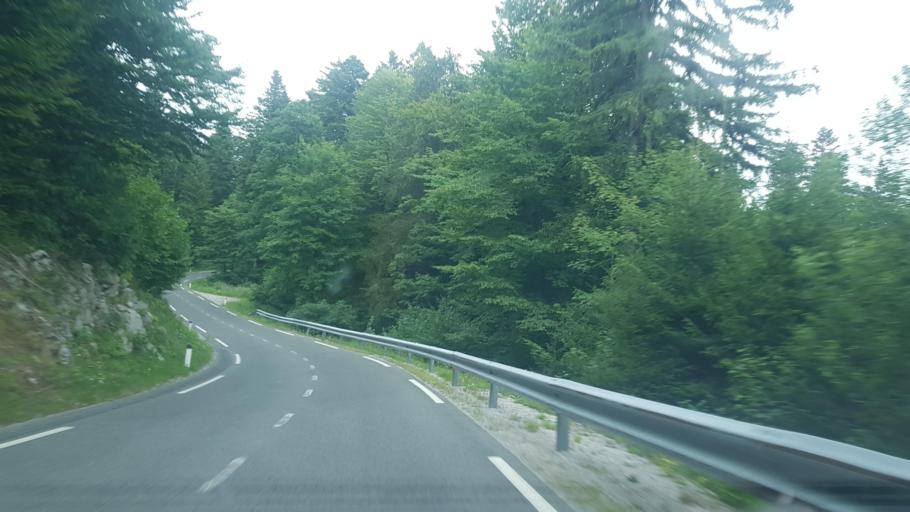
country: SI
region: Logatec
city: Logatec
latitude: 45.8685
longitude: 14.1251
